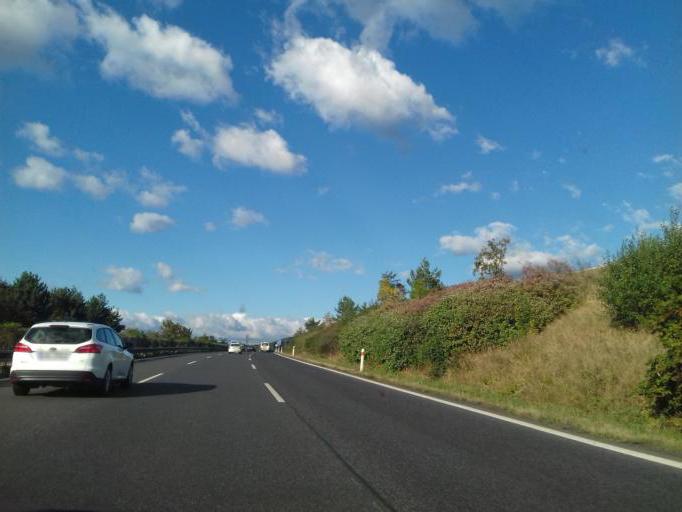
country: CZ
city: Ohrazenice
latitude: 50.6278
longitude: 15.1089
